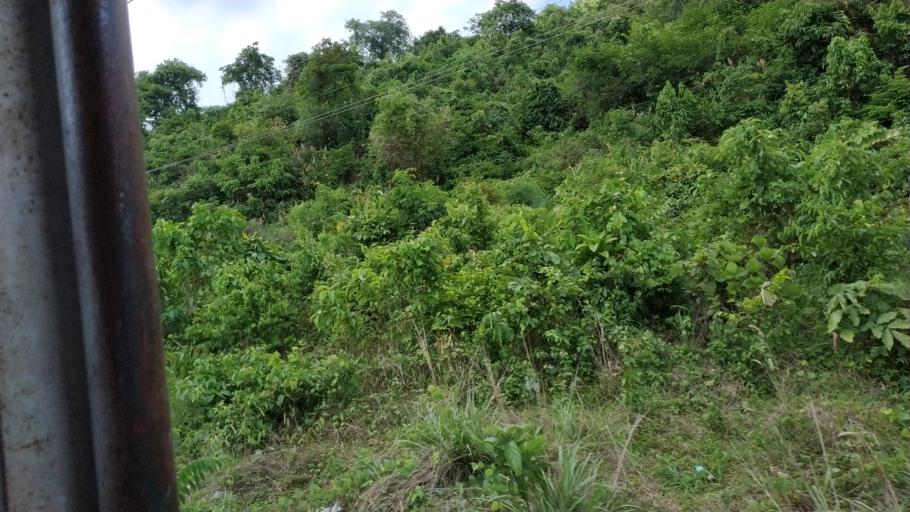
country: MM
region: Mon
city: Kyaikto
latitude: 17.4140
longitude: 97.0722
